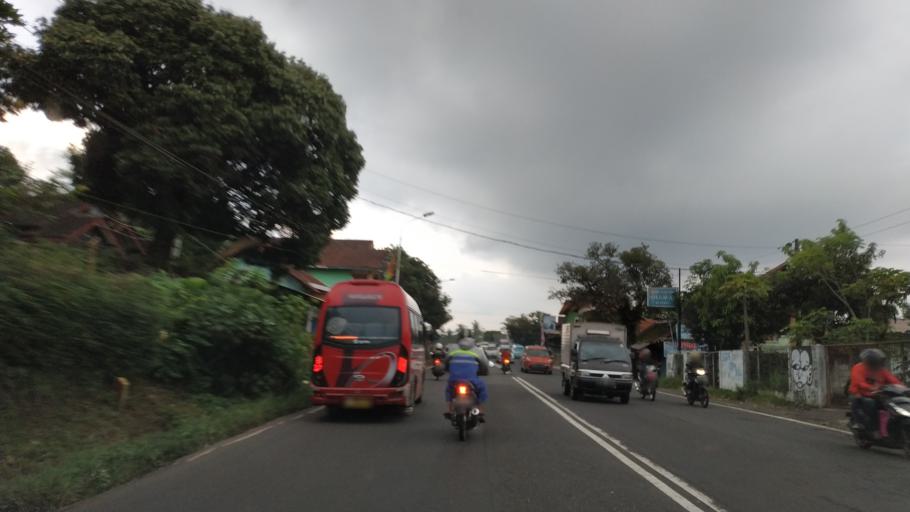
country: ID
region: Central Java
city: Salatiga
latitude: -7.2904
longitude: 110.4658
